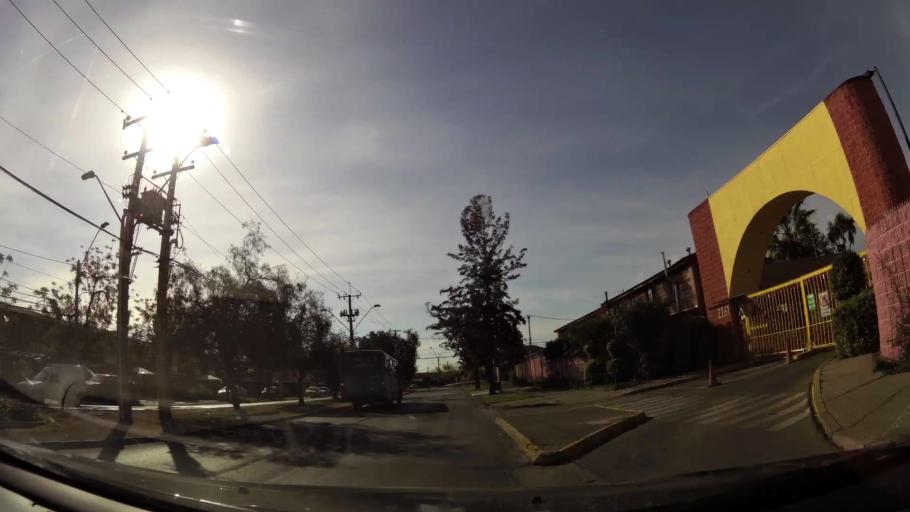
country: CL
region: Santiago Metropolitan
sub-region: Provincia de Cordillera
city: Puente Alto
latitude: -33.5890
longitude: -70.5623
